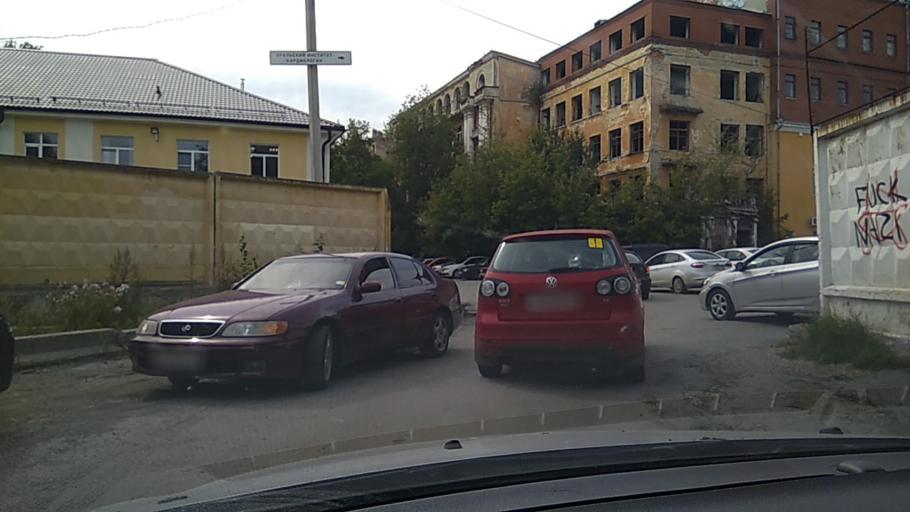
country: RU
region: Sverdlovsk
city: Yekaterinburg
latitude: 56.8205
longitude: 60.6012
